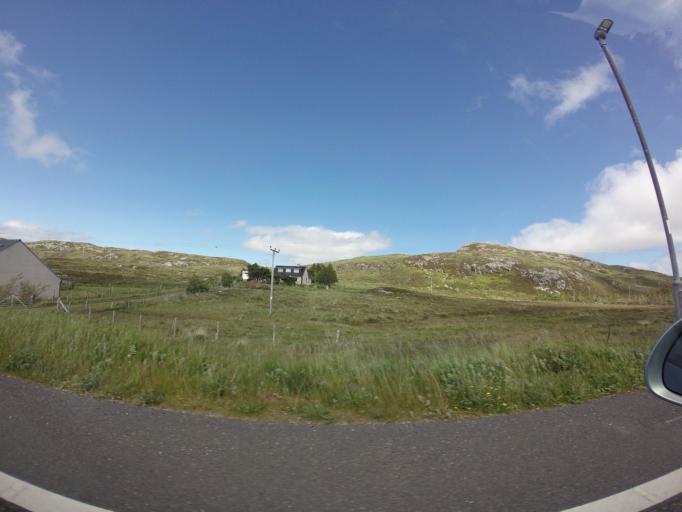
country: GB
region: Scotland
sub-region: Eilean Siar
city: Stornoway
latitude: 58.1065
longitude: -6.5306
